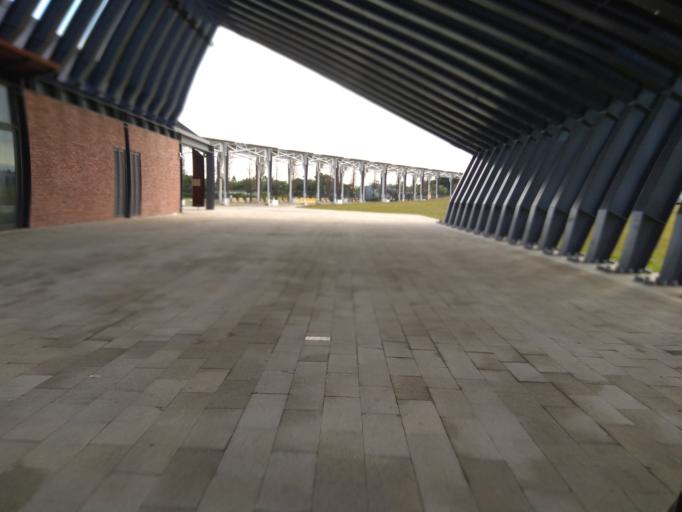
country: TW
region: Taiwan
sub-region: Hsinchu
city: Zhubei
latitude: 25.0080
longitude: 121.0481
